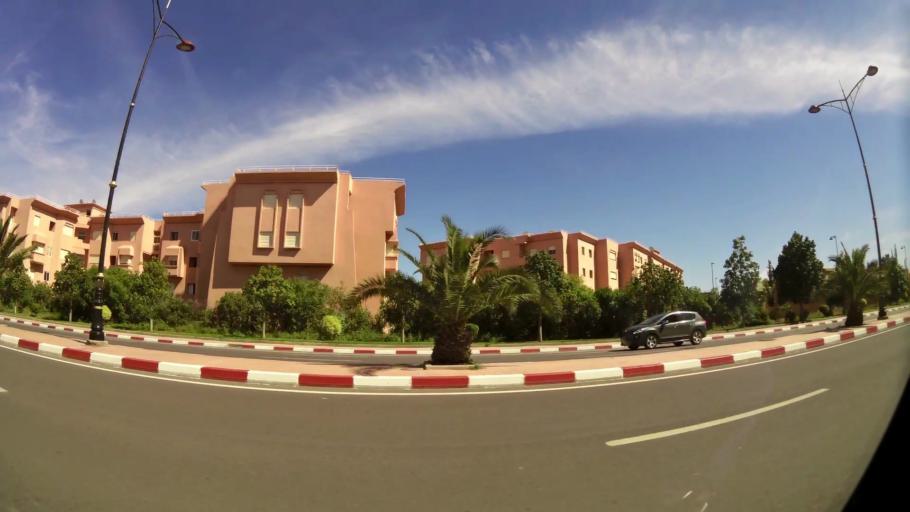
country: MA
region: Marrakech-Tensift-Al Haouz
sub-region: Marrakech
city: Marrakesh
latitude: 31.6735
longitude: -8.0054
